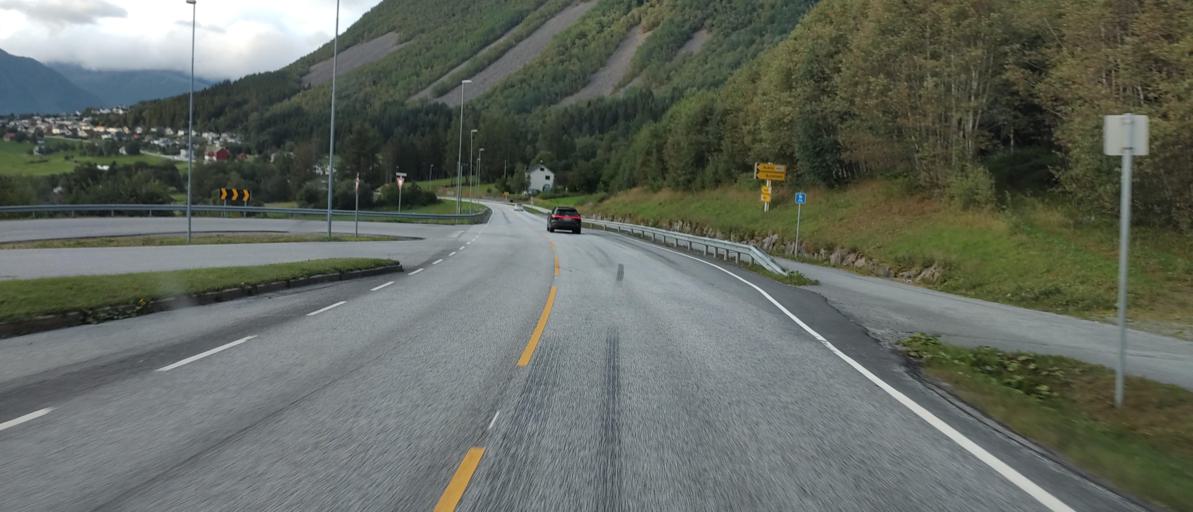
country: NO
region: More og Romsdal
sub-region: Molde
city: Molde
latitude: 62.8022
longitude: 7.2448
